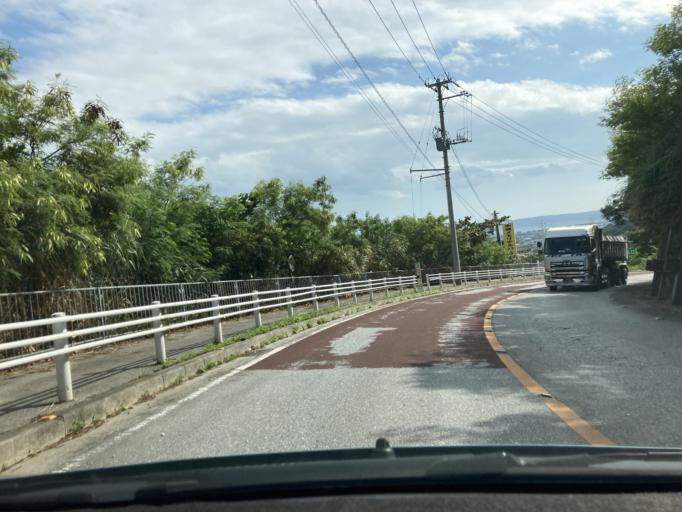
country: JP
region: Okinawa
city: Ginowan
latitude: 26.2660
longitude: 127.7861
